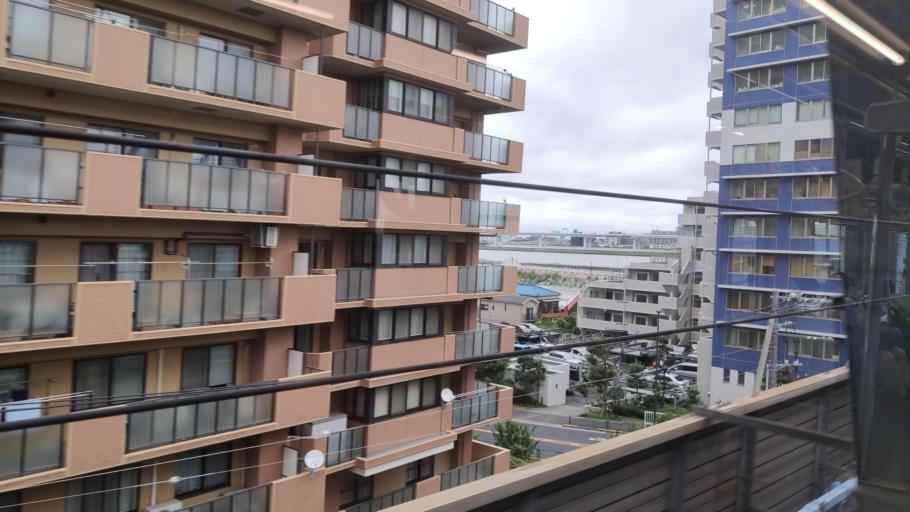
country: JP
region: Tokyo
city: Urayasu
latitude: 35.6662
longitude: 139.8414
